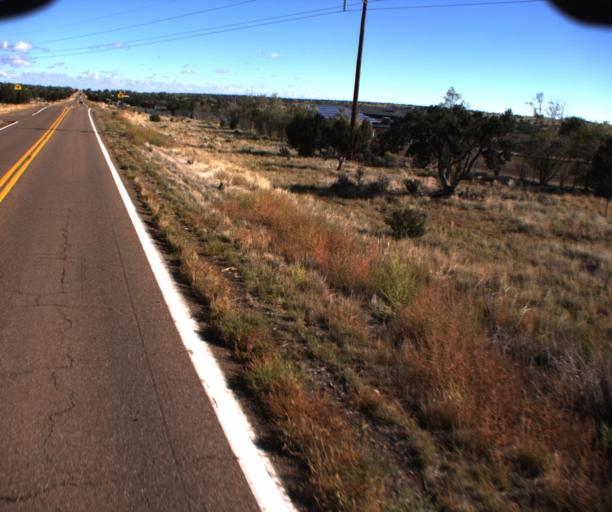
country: US
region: Arizona
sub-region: Apache County
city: Saint Johns
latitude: 34.4214
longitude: -109.6421
